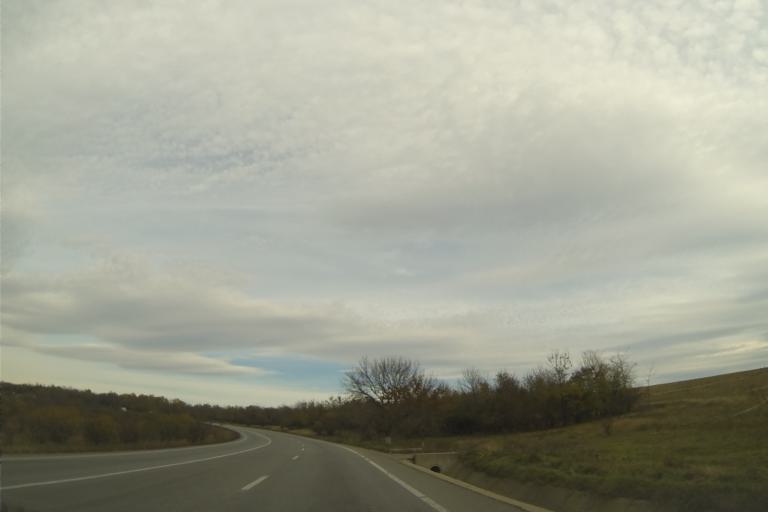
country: RO
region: Olt
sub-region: Comuna Valea Mare
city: Valea Mare
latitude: 44.4837
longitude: 24.4415
